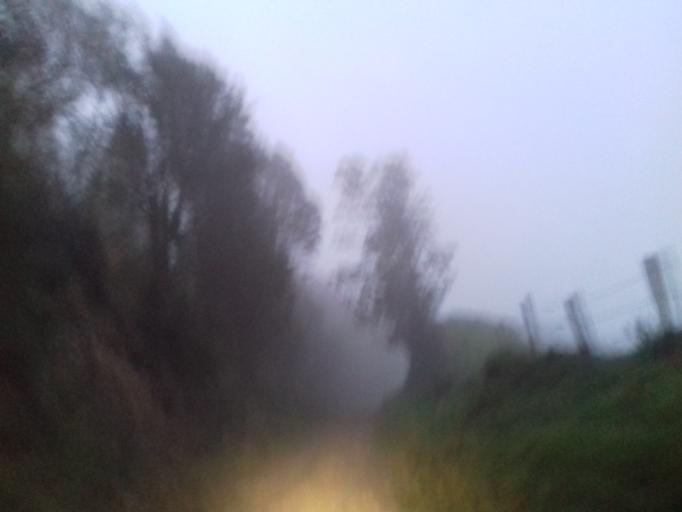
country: CO
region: Quindio
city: Salento
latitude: 4.5776
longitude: -75.5258
